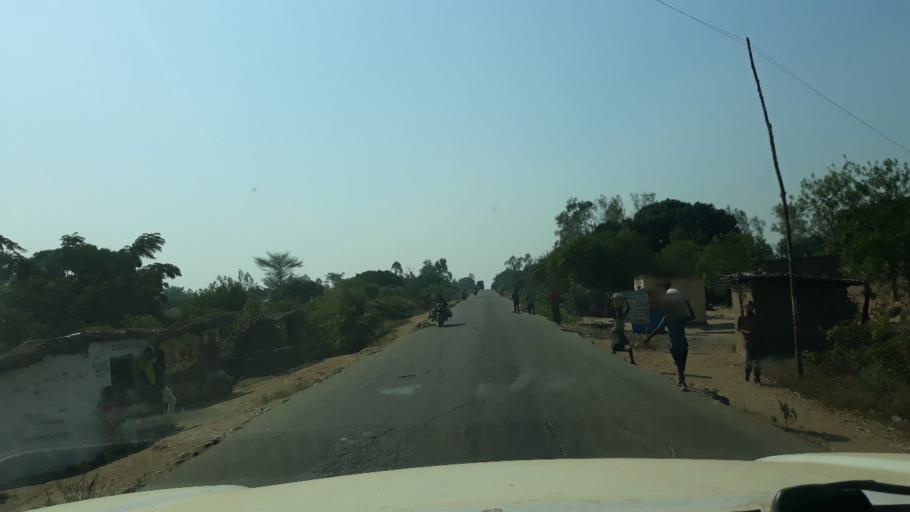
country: BI
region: Cibitoke
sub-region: Commune of Buganda
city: Buganda
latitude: -3.0698
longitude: 29.1217
